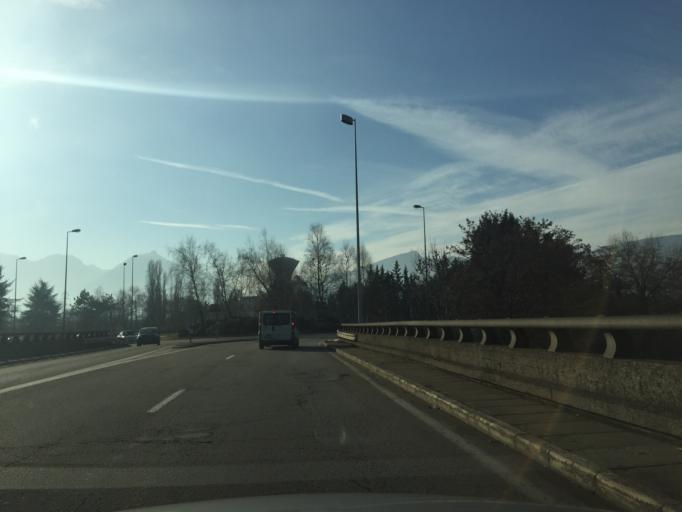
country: FR
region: Rhone-Alpes
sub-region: Departement de la Savoie
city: Cognin
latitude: 45.5866
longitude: 5.9078
